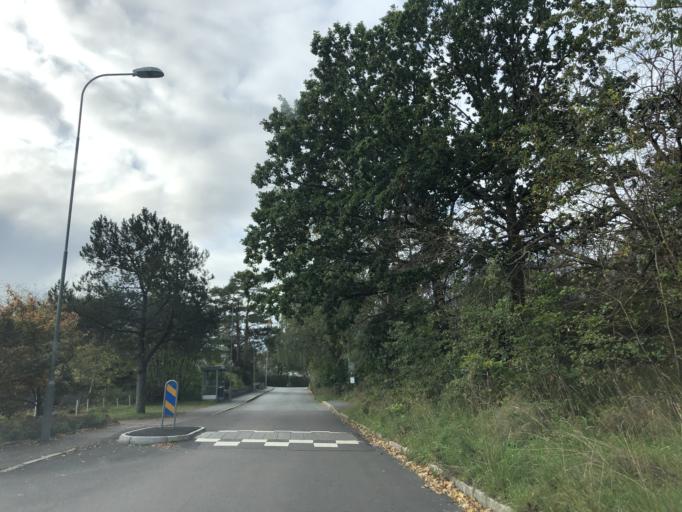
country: SE
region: Vaestra Goetaland
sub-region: Goteborg
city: Majorna
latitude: 57.6781
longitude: 11.8713
